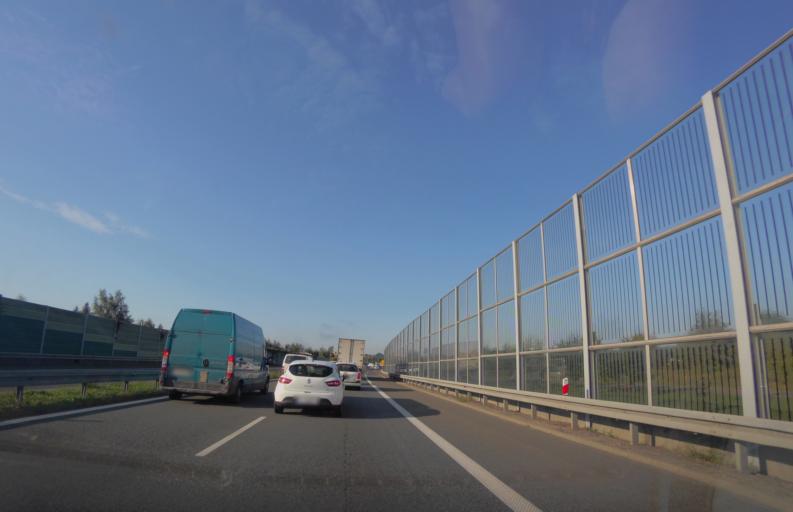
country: PL
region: Subcarpathian Voivodeship
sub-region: Powiat rzeszowski
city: Trzebownisko
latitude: 50.0580
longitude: 22.0404
